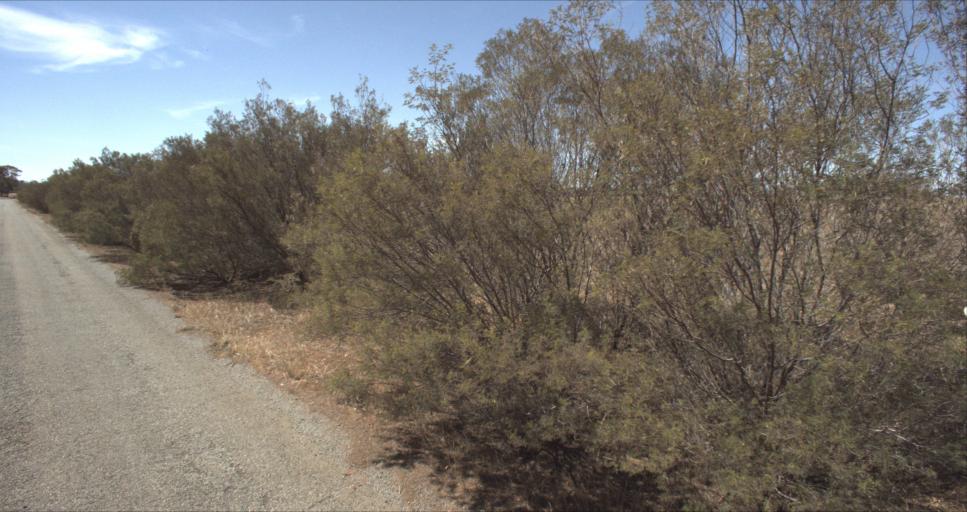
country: AU
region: New South Wales
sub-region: Leeton
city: Leeton
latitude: -34.5909
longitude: 146.4408
